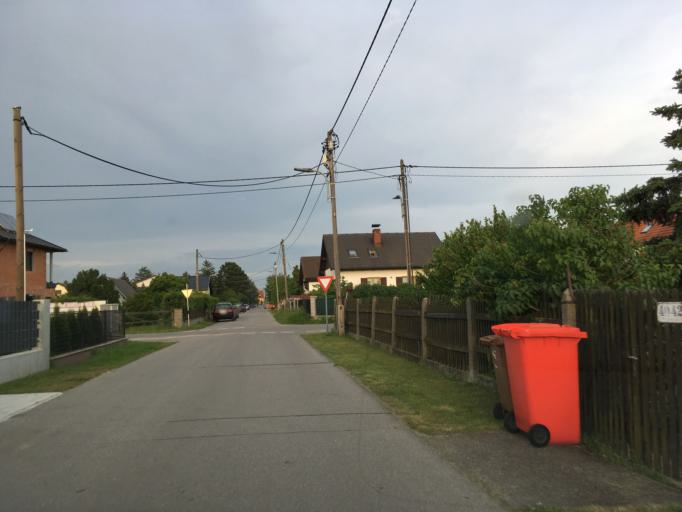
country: AT
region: Lower Austria
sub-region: Politischer Bezirk Wien-Umgebung
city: Gerasdorf bei Wien
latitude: 48.3176
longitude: 16.4987
